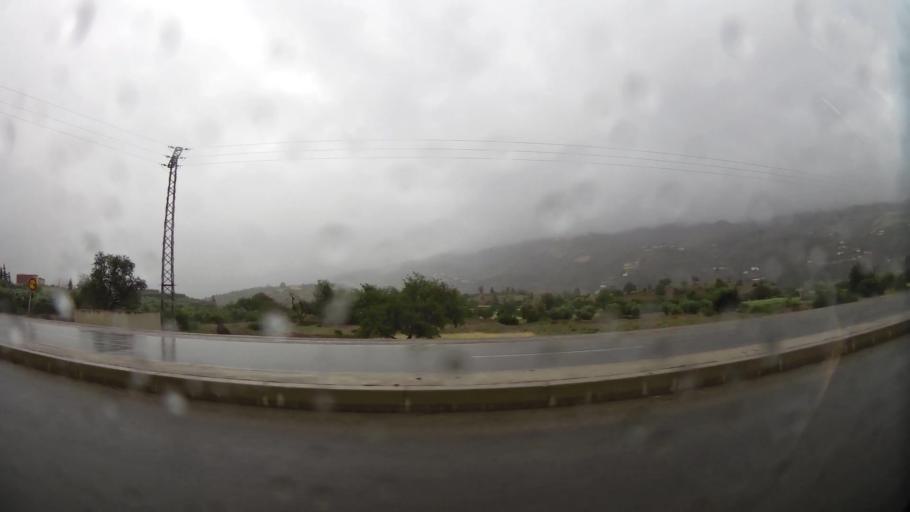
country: MA
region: Taza-Al Hoceima-Taounate
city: Imzourene
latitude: 35.0445
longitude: -3.8239
